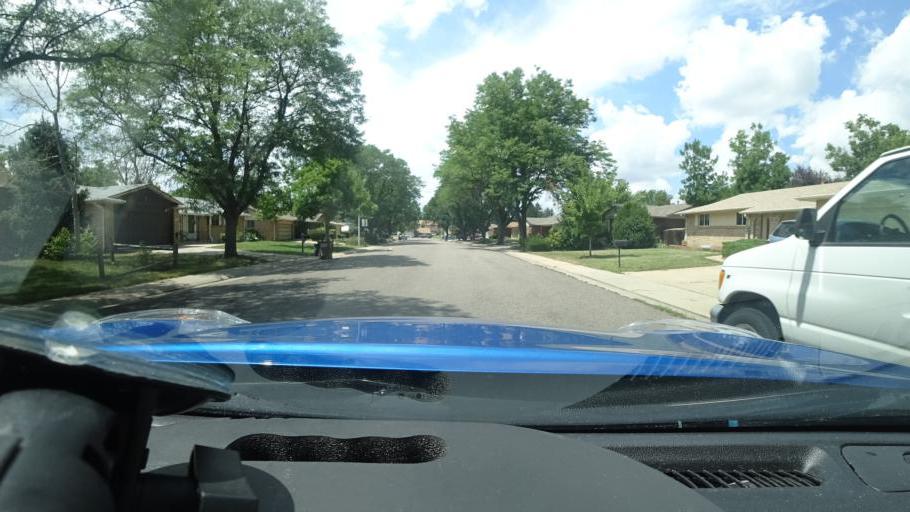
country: US
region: Colorado
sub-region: Adams County
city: Aurora
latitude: 39.7005
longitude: -104.8420
